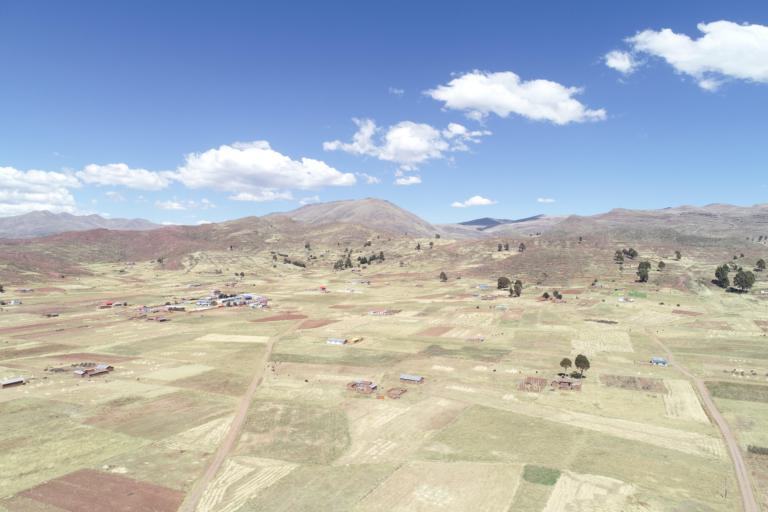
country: BO
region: La Paz
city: Tiahuanaco
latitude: -16.5944
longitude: -68.7720
